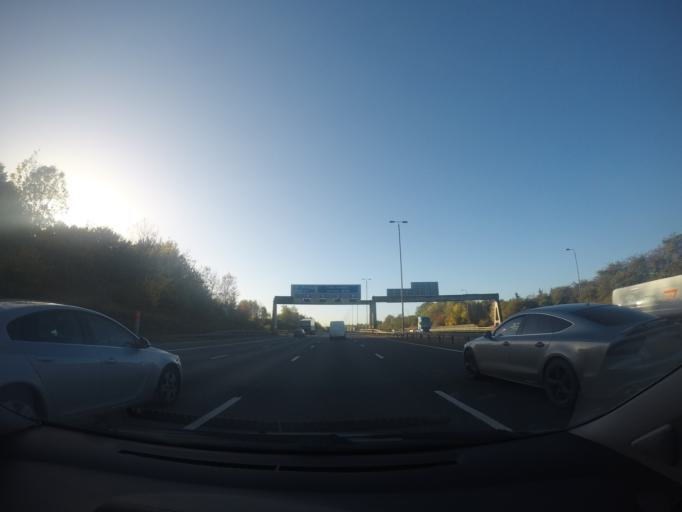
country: GB
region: England
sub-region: City and Borough of Leeds
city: Aberford
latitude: 53.8264
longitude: -1.3382
